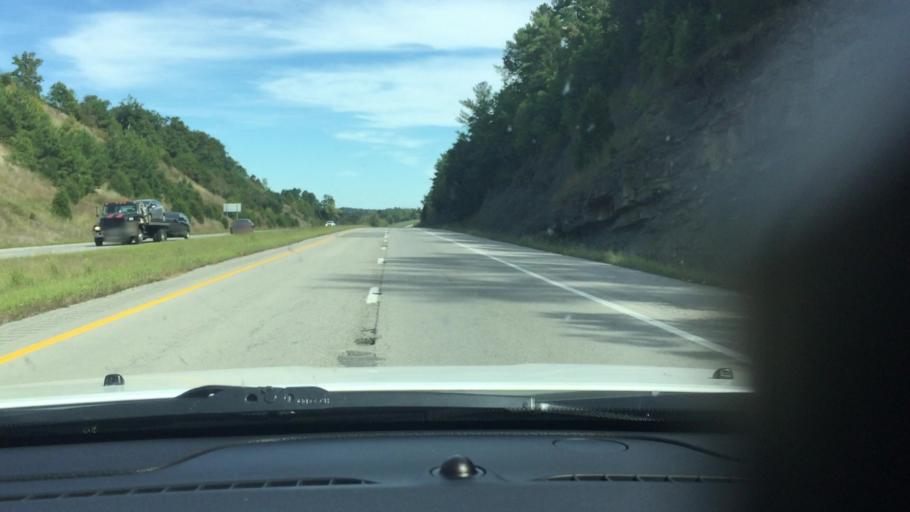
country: US
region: Kentucky
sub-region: Caldwell County
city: Princeton
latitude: 37.1402
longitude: -87.8331
